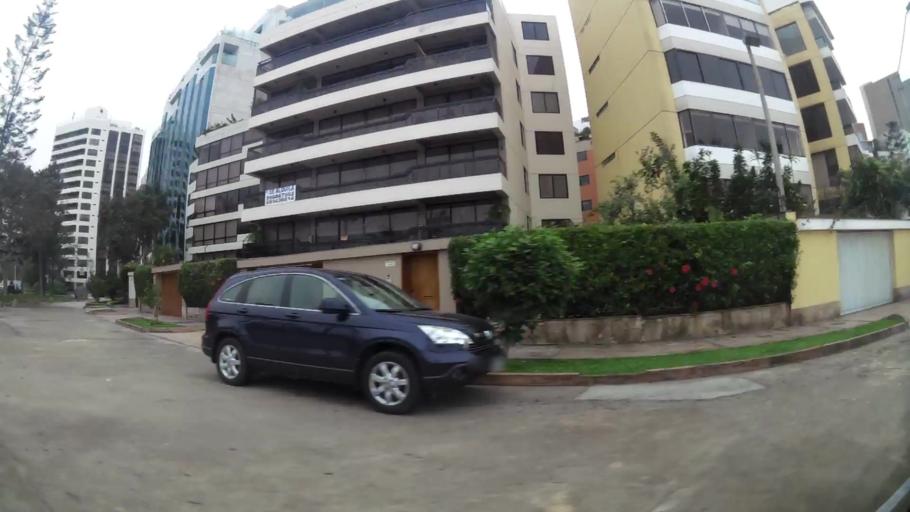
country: PE
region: Lima
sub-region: Lima
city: Surco
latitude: -12.1358
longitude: -77.0280
